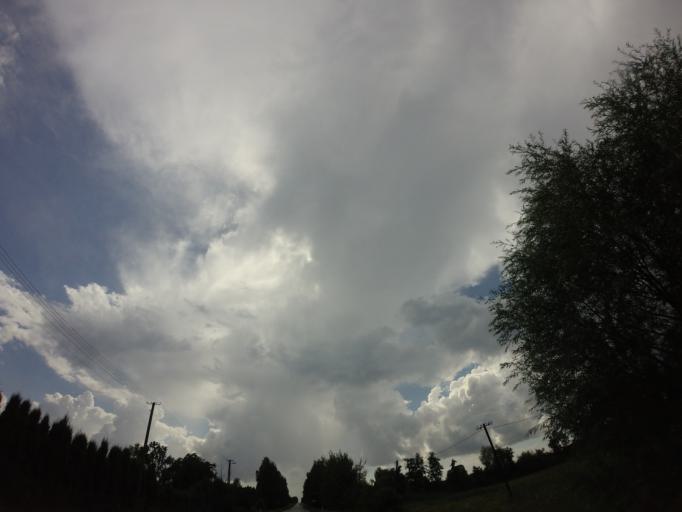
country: PL
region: Swietokrzyskie
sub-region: Powiat buski
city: Tuczepy
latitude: 50.4591
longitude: 20.9981
